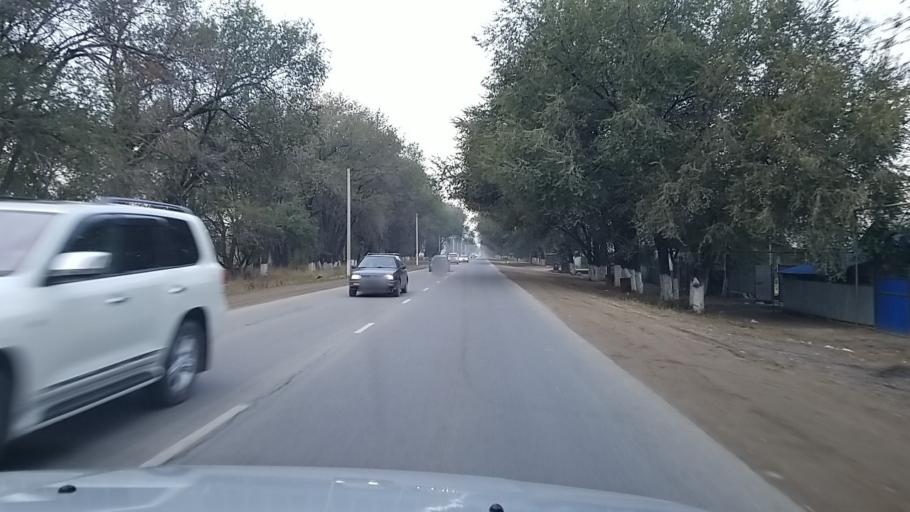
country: KZ
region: Almaty Oblysy
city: Burunday
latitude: 43.3549
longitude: 76.8102
